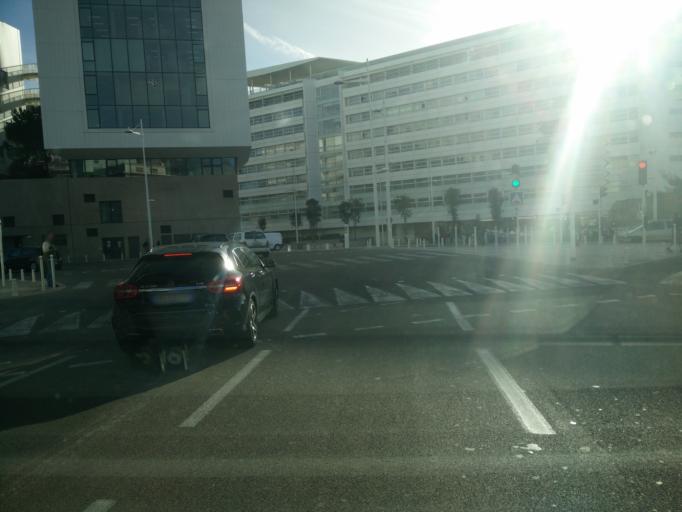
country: FR
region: Provence-Alpes-Cote d'Azur
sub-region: Departement du Var
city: Toulon
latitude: 43.1217
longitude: 5.9391
